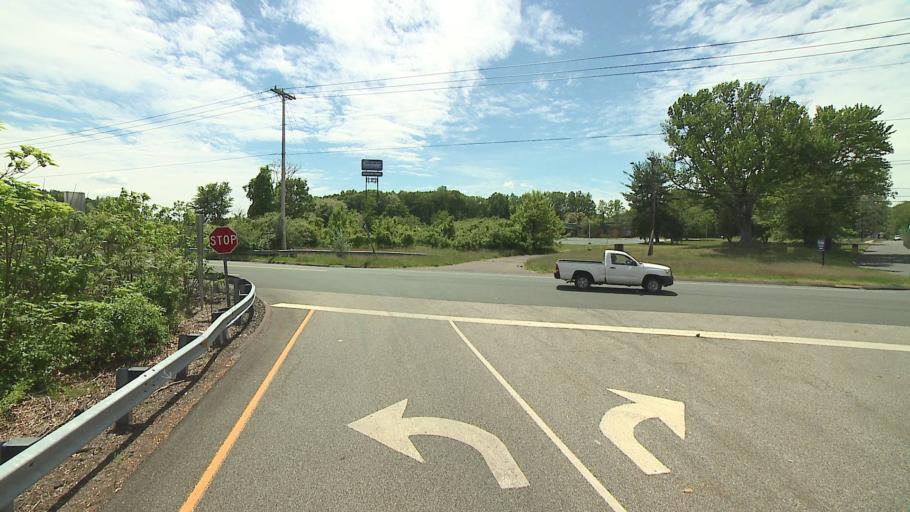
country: US
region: Connecticut
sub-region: Hartford County
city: Windsor Locks
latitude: 41.9051
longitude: -72.6351
